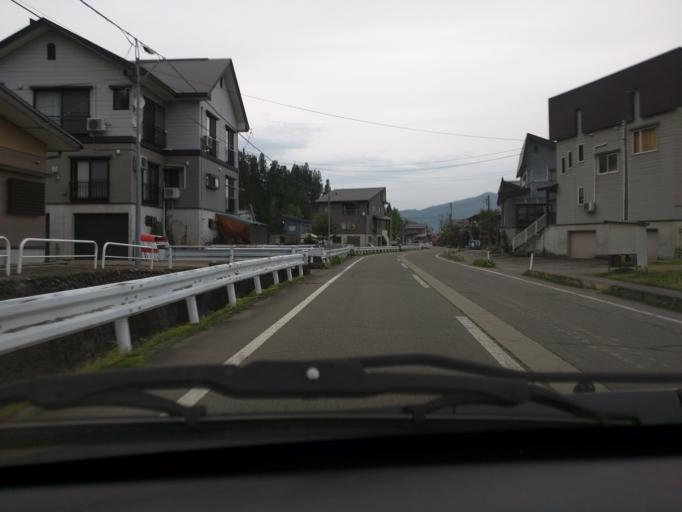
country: JP
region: Niigata
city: Muikamachi
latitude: 37.2198
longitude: 138.9506
